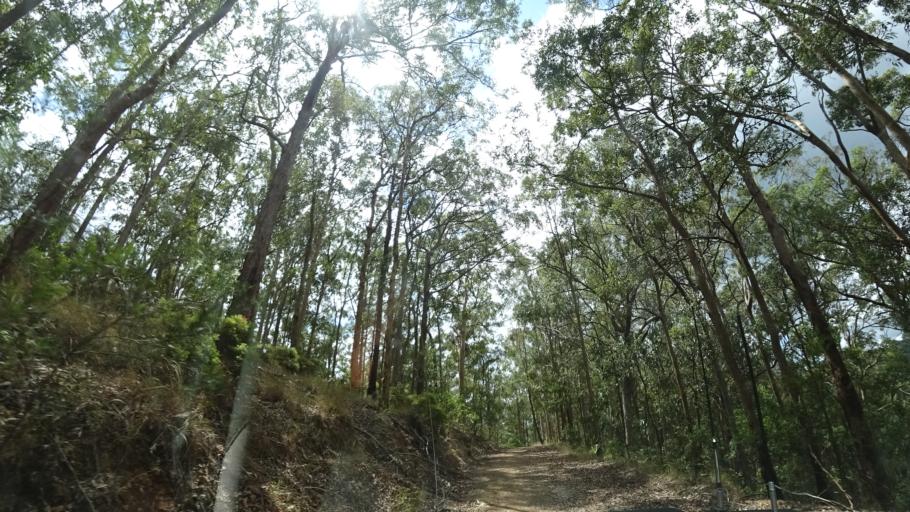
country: AU
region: Queensland
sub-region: Moreton Bay
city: Highvale
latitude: -27.3918
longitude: 152.7424
